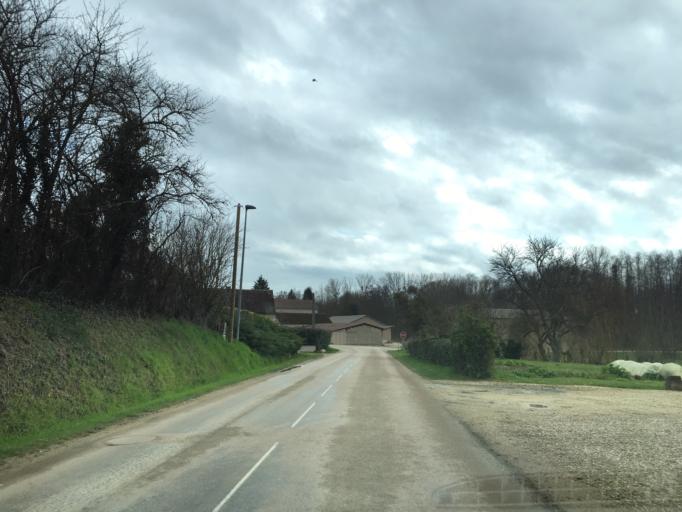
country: FR
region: Bourgogne
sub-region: Departement de l'Yonne
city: Pourrain
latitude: 47.7966
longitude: 3.3828
